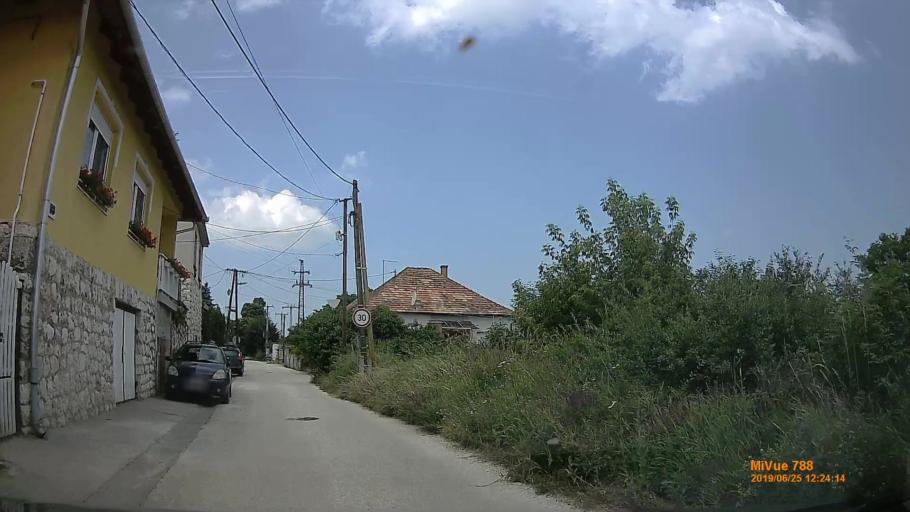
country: HU
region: Komarom-Esztergom
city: Dorog
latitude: 47.7187
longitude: 18.7260
